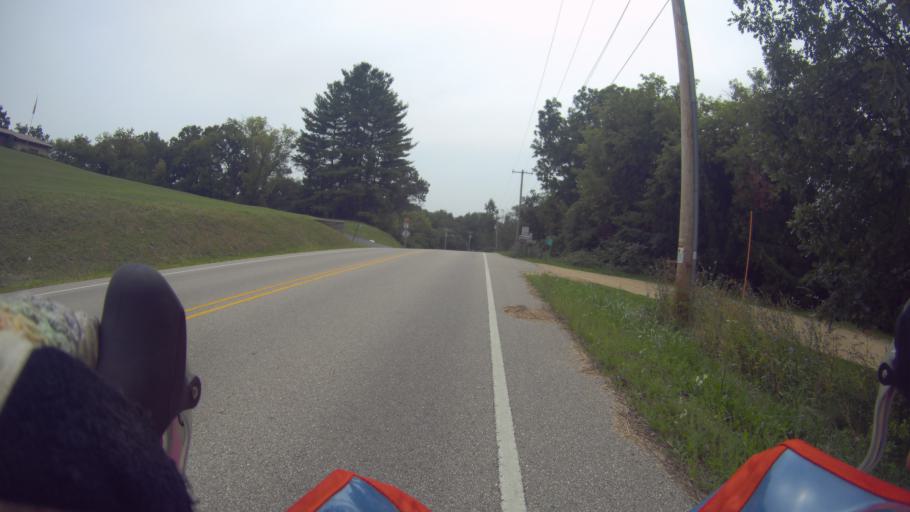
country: US
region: Wisconsin
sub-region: Dane County
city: Mount Horeb
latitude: 42.9500
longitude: -89.6593
